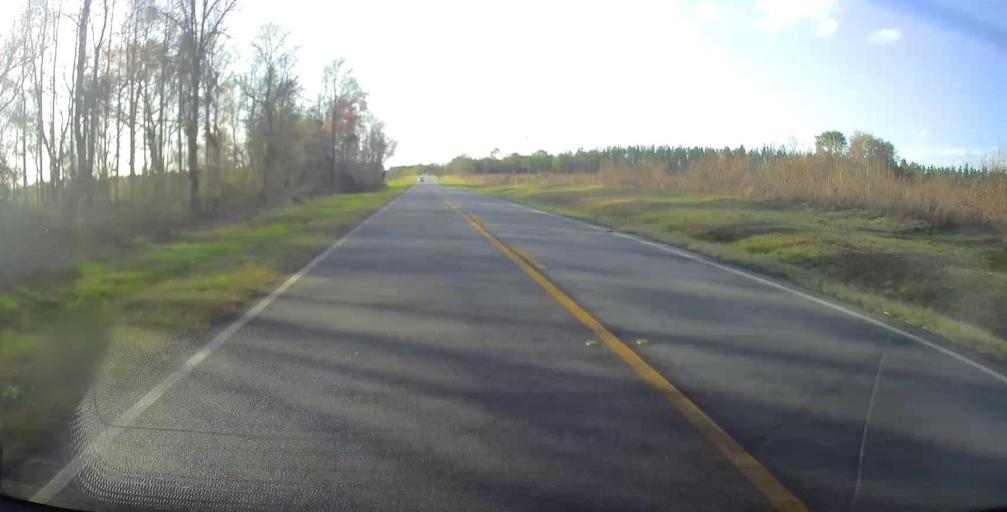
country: US
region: Georgia
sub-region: Tattnall County
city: Reidsville
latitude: 32.1325
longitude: -82.2218
